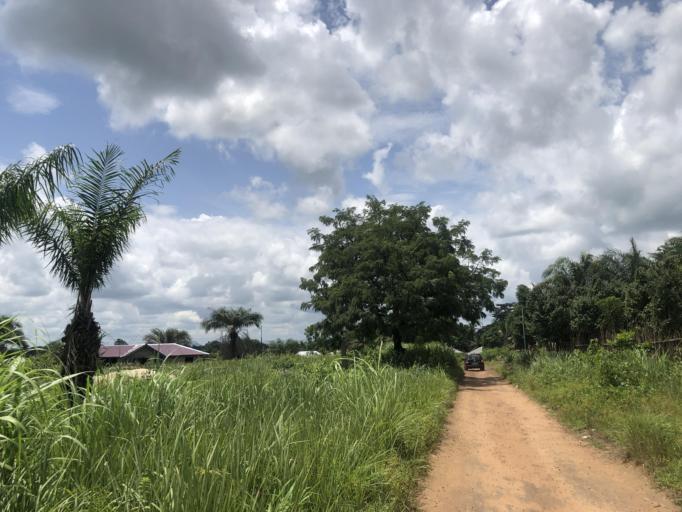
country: SL
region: Northern Province
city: Magburaka
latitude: 8.7094
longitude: -11.9339
